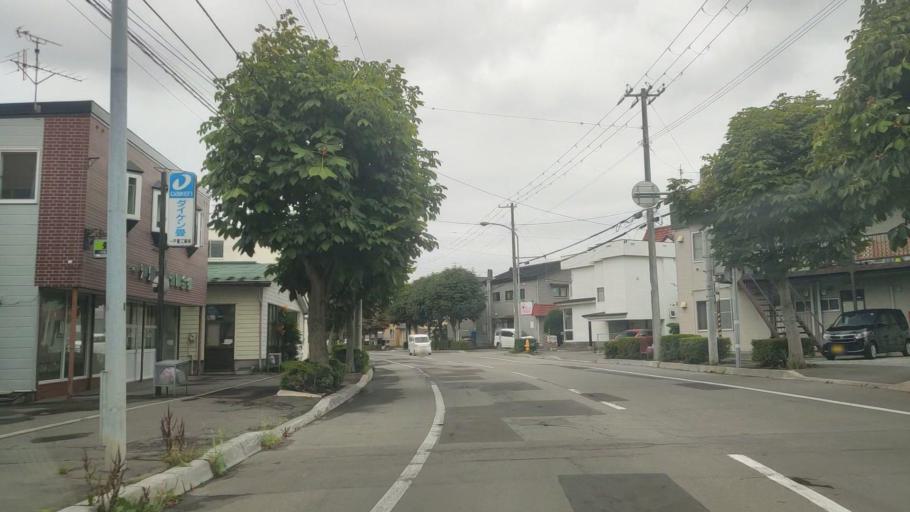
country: JP
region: Hokkaido
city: Hakodate
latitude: 41.7980
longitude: 140.7619
